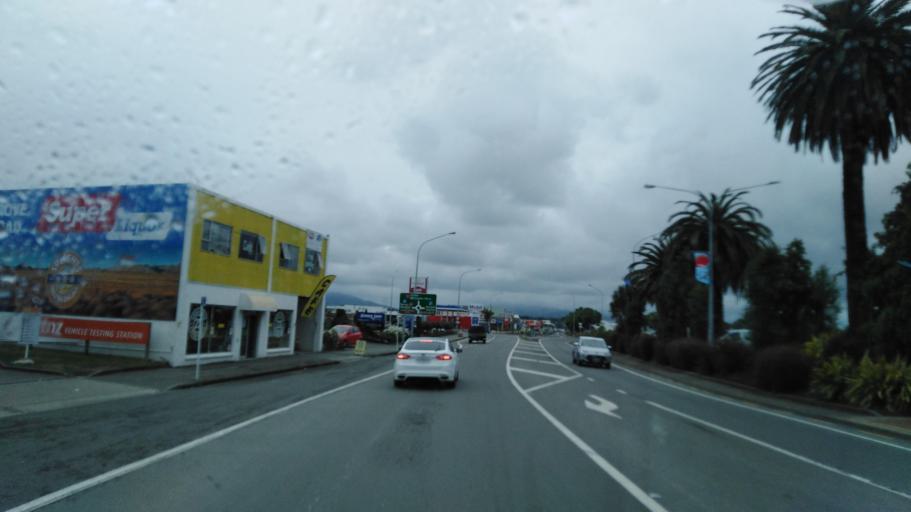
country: NZ
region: Marlborough
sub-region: Marlborough District
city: Blenheim
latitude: -41.5092
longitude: 173.9592
